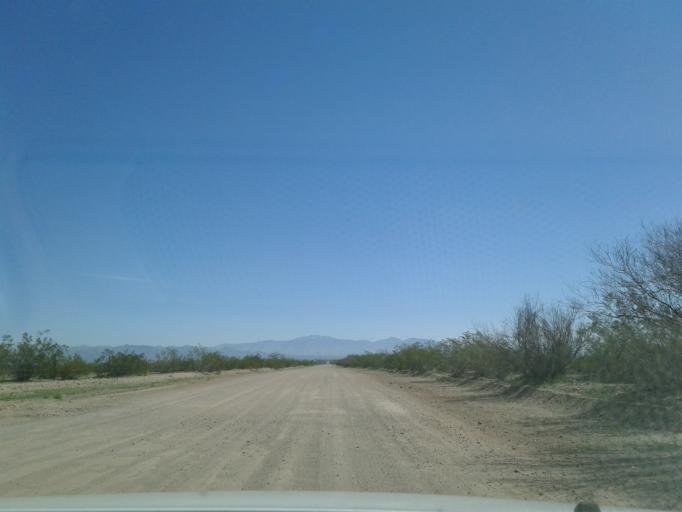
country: US
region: Arizona
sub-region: Pima County
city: Avra Valley
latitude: 32.4293
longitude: -111.3596
